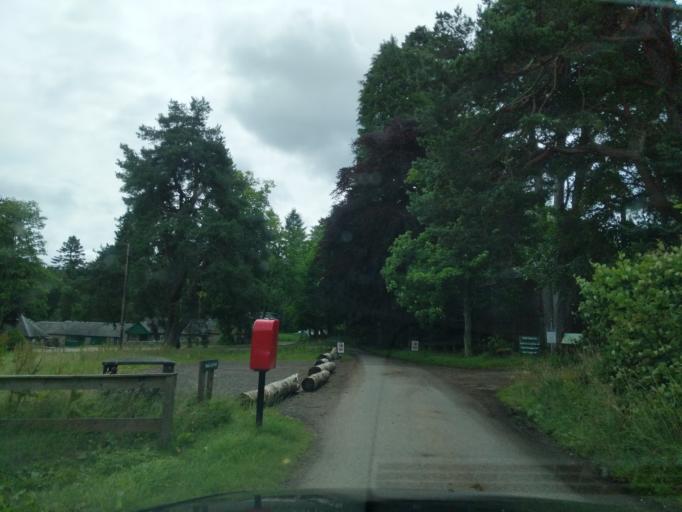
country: GB
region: Scotland
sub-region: Aberdeenshire
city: Aboyne
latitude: 57.0489
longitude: -2.8690
